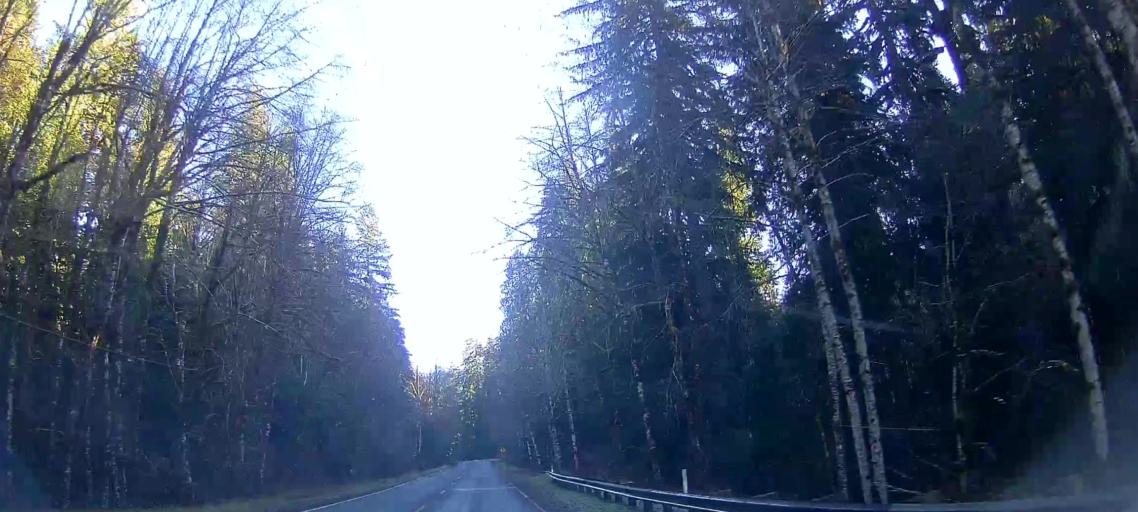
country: US
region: Washington
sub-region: Snohomish County
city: Darrington
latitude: 48.6478
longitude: -121.7229
